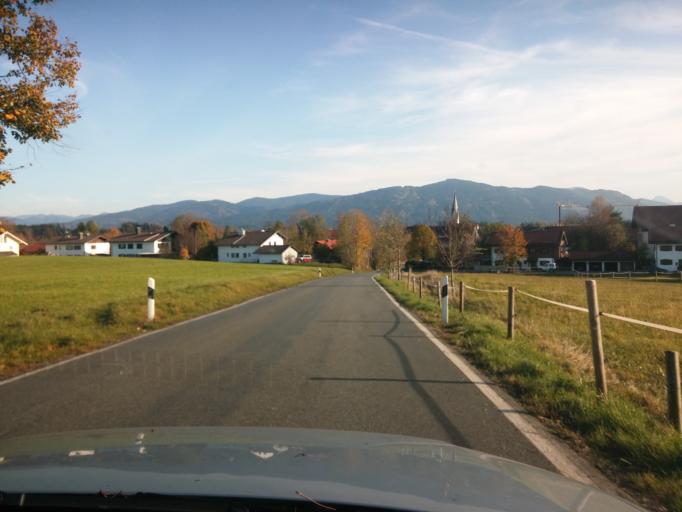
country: DE
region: Bavaria
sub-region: Upper Bavaria
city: Bad Toelz
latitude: 47.7849
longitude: 11.5836
